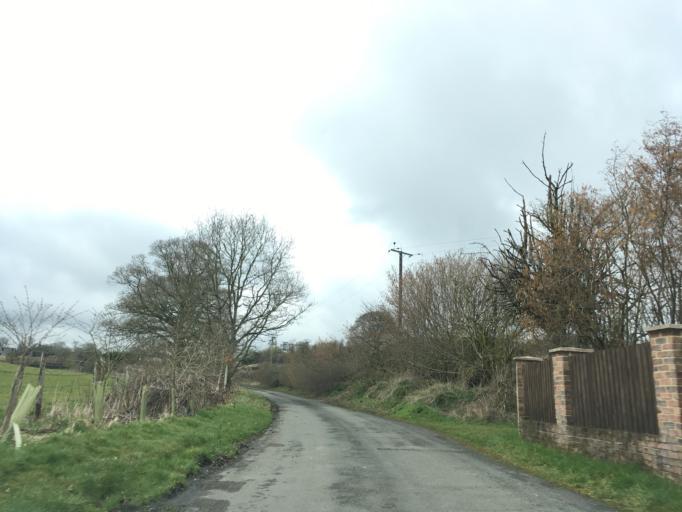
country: GB
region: England
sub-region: West Berkshire
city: Lambourn
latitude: 51.4777
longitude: -1.5385
